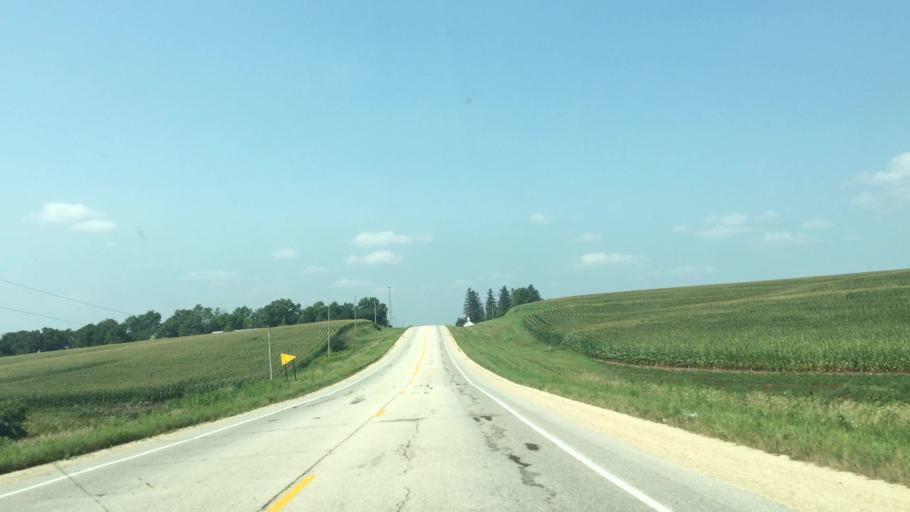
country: US
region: Minnesota
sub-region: Fillmore County
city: Harmony
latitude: 43.6551
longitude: -91.9301
